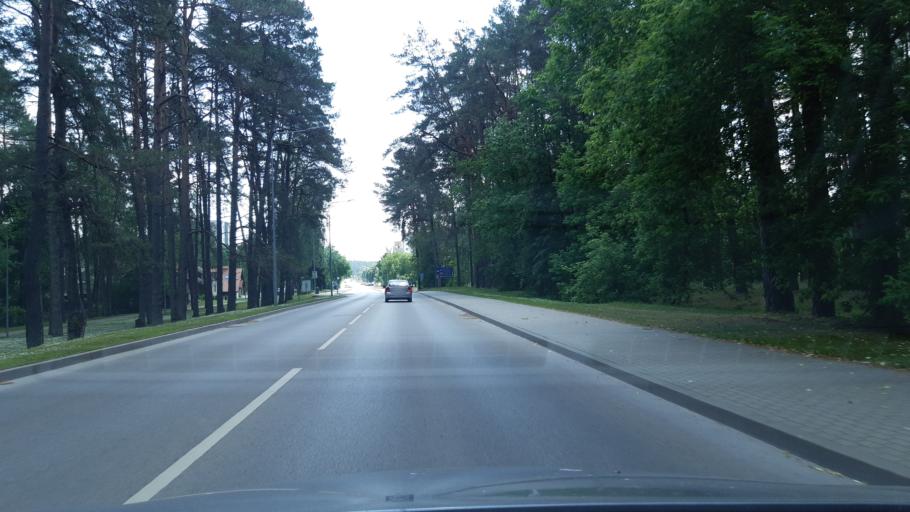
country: LT
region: Alytaus apskritis
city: Druskininkai
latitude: 54.0073
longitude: 23.9805
